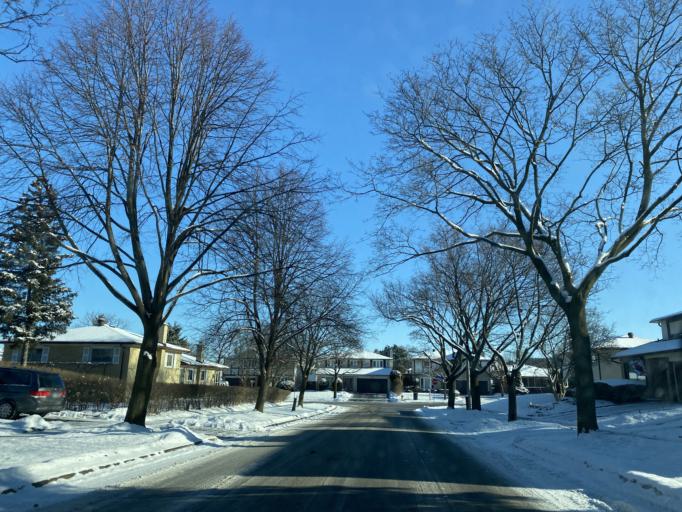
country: CA
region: Ontario
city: Scarborough
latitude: 43.7831
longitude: -79.3071
